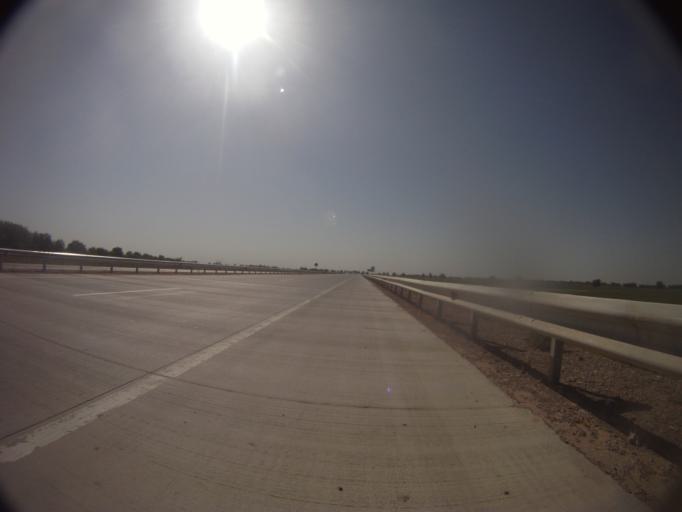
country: KZ
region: Ongtustik Qazaqstan
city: Turkestan
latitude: 43.1864
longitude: 68.4951
